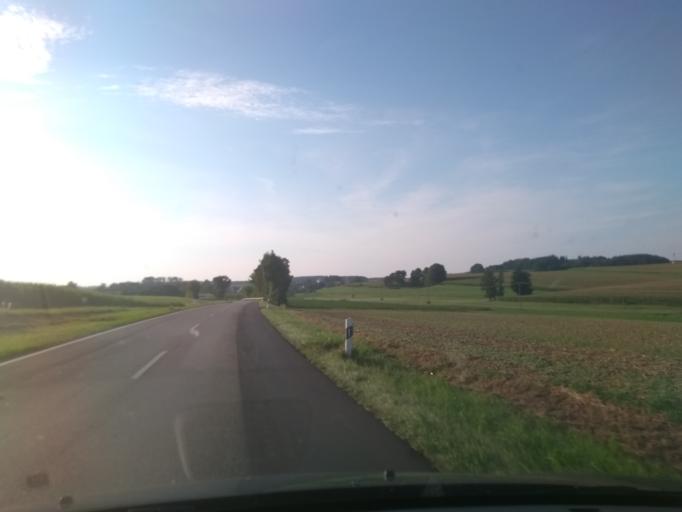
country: DE
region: Bavaria
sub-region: Upper Bavaria
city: Markt Indersdorf
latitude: 48.3747
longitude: 11.3641
